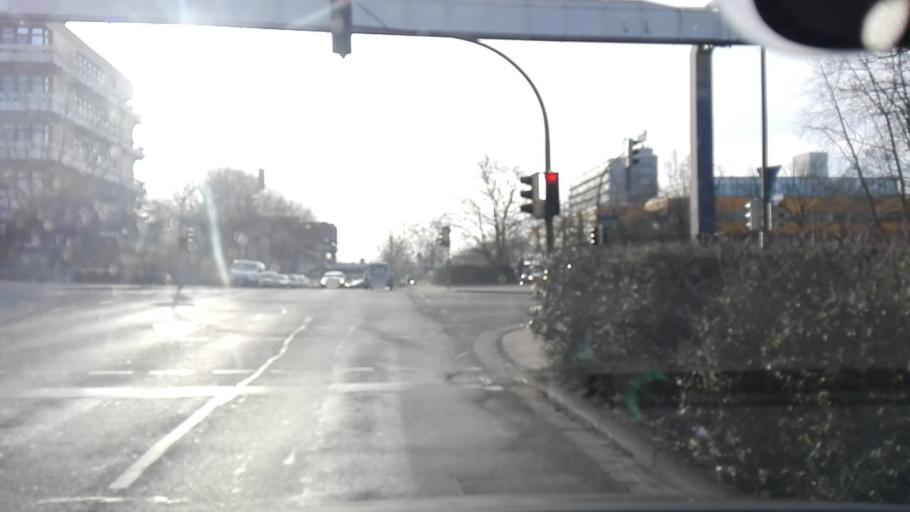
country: DE
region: North Rhine-Westphalia
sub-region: Regierungsbezirk Arnsberg
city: Dortmund
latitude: 51.4948
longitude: 7.4153
